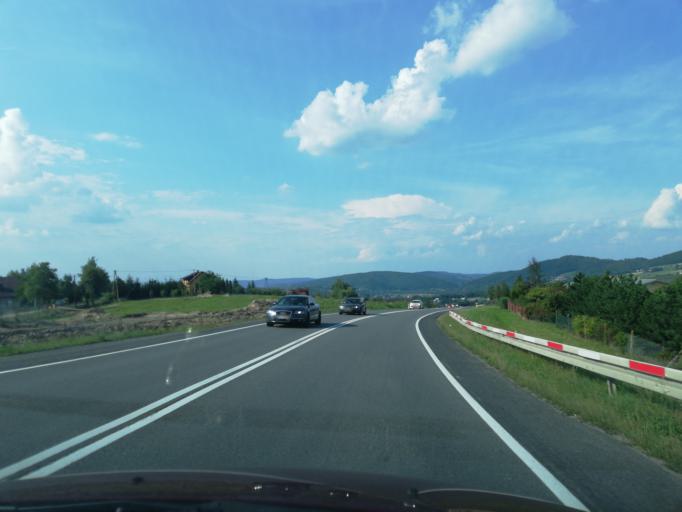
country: PL
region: Lesser Poland Voivodeship
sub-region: Powiat nowosadecki
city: Lososina Dolna
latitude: 49.7281
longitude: 20.6388
